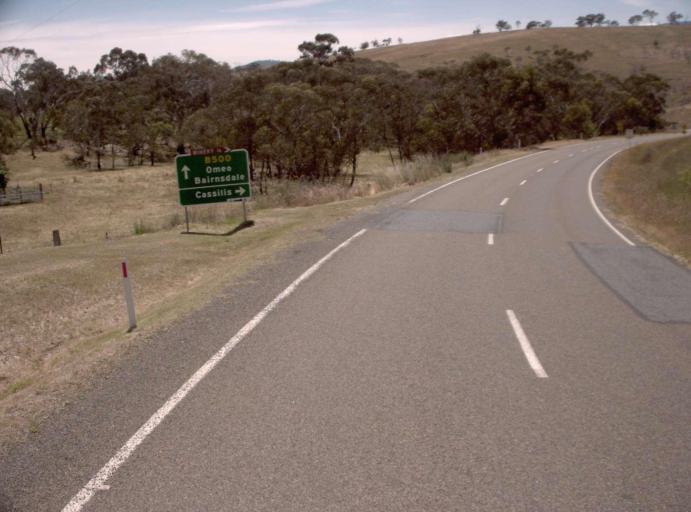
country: AU
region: Victoria
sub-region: Alpine
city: Mount Beauty
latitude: -37.1133
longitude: 147.5728
